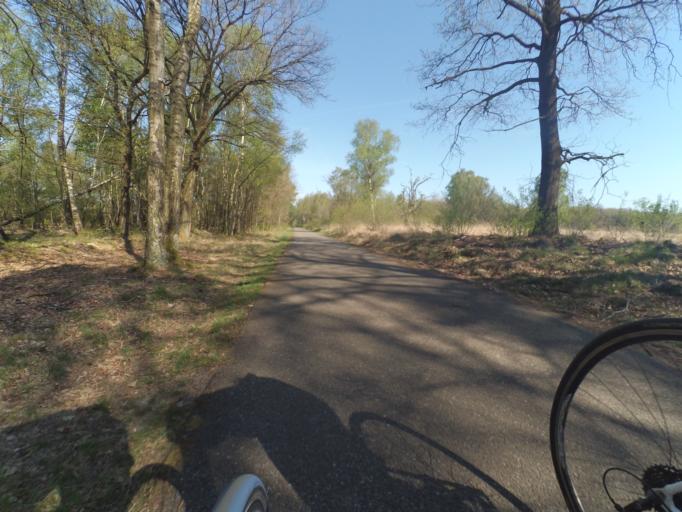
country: NL
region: Gelderland
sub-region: Gemeente Ede
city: Harskamp
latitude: 52.1838
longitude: 5.8133
